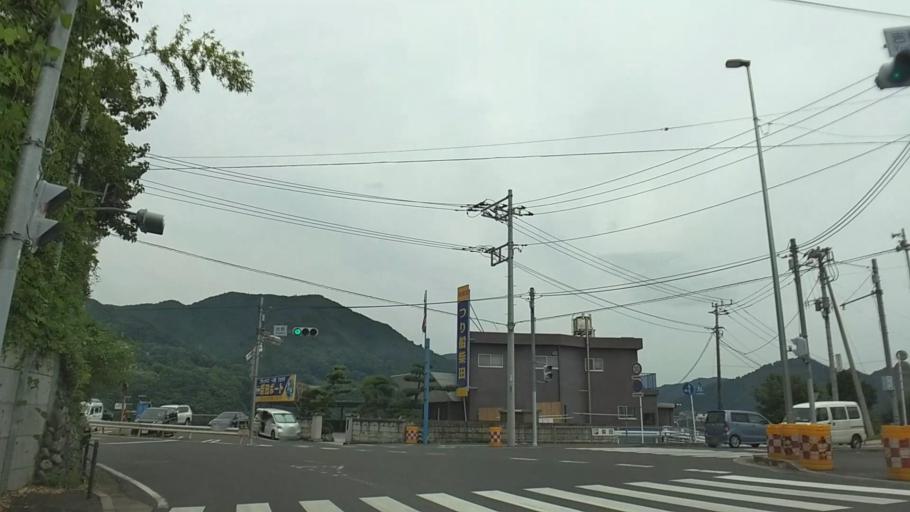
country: JP
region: Yamanashi
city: Uenohara
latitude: 35.6145
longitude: 139.1710
